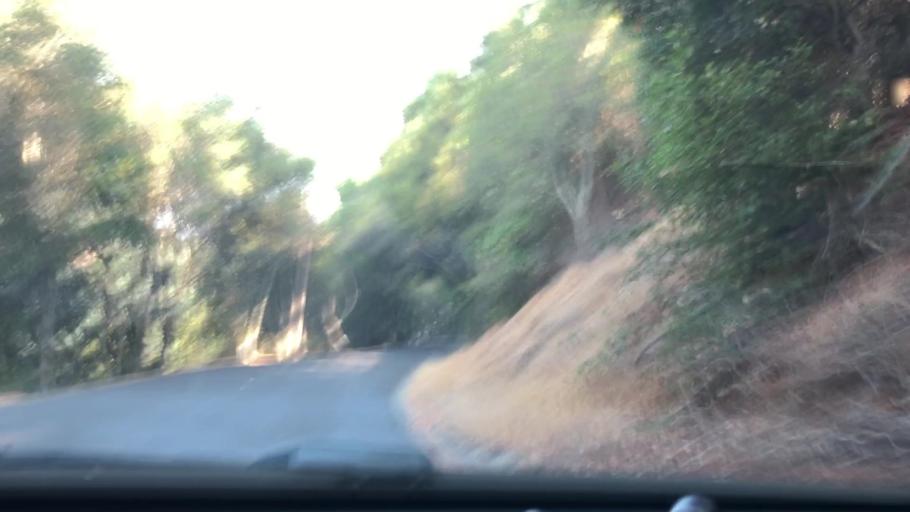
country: US
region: California
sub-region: Contra Costa County
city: Orinda
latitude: 37.9161
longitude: -122.1593
